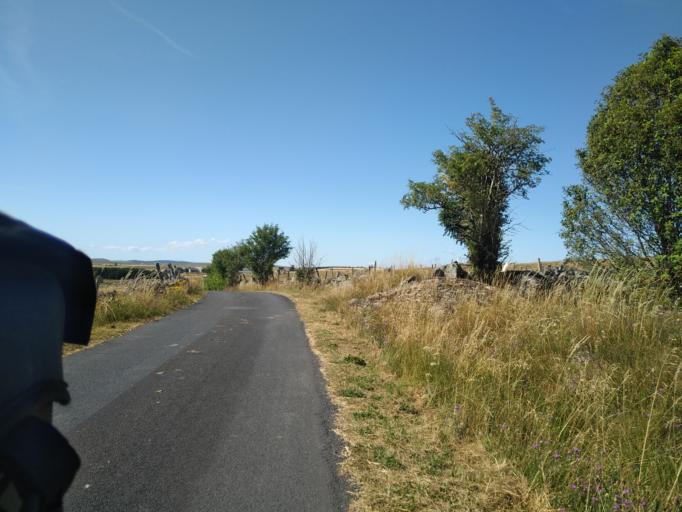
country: FR
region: Languedoc-Roussillon
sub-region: Departement de la Lozere
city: Aumont-Aubrac
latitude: 44.6763
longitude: 3.0976
